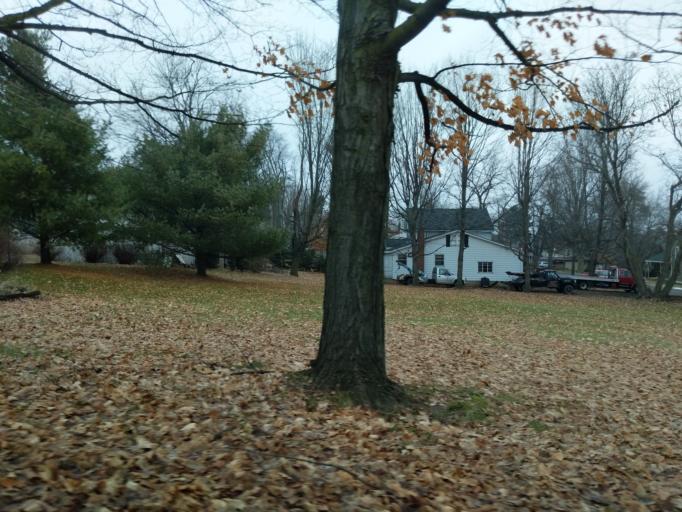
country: US
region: Michigan
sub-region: Lapeer County
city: Barnes Lake-Millers Lake
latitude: 43.3322
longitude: -83.3518
